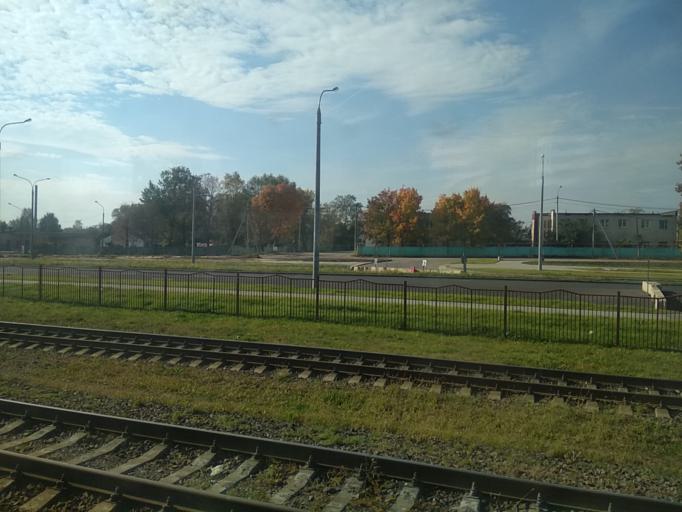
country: BY
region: Minsk
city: Minsk
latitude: 53.8658
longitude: 27.5605
